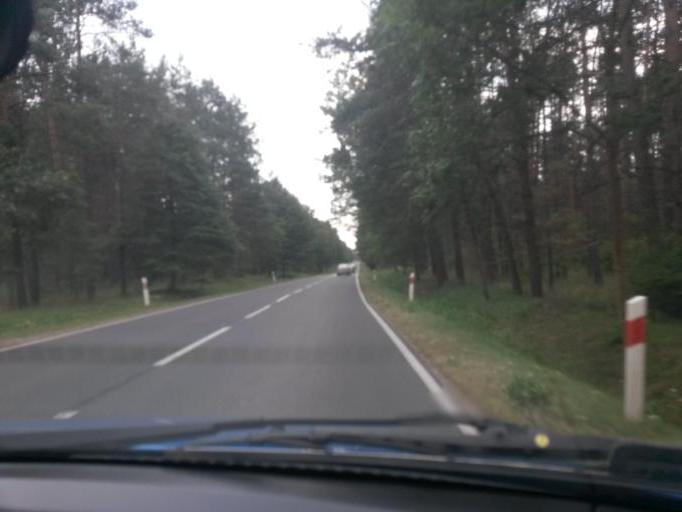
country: PL
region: Masovian Voivodeship
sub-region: Powiat zurominski
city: Lubowidz
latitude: 53.1408
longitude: 19.8411
